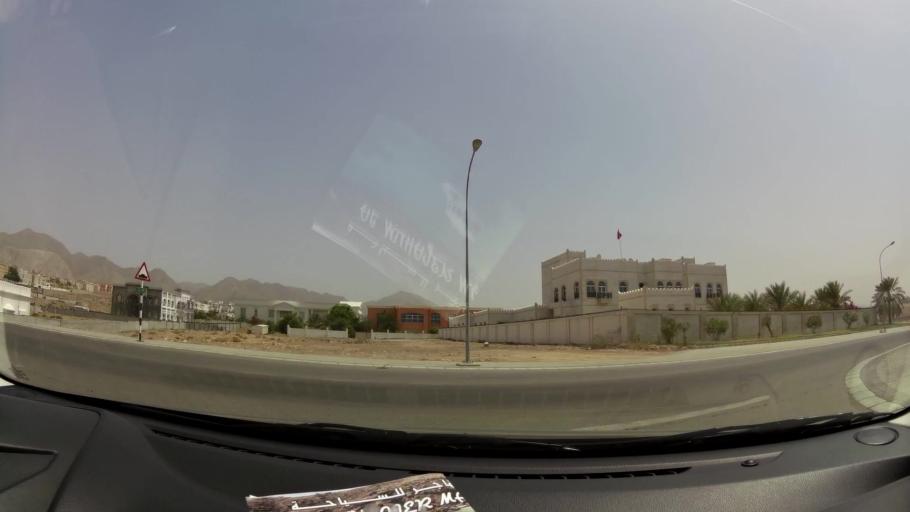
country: OM
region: Muhafazat Masqat
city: Bawshar
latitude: 23.5621
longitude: 58.3957
